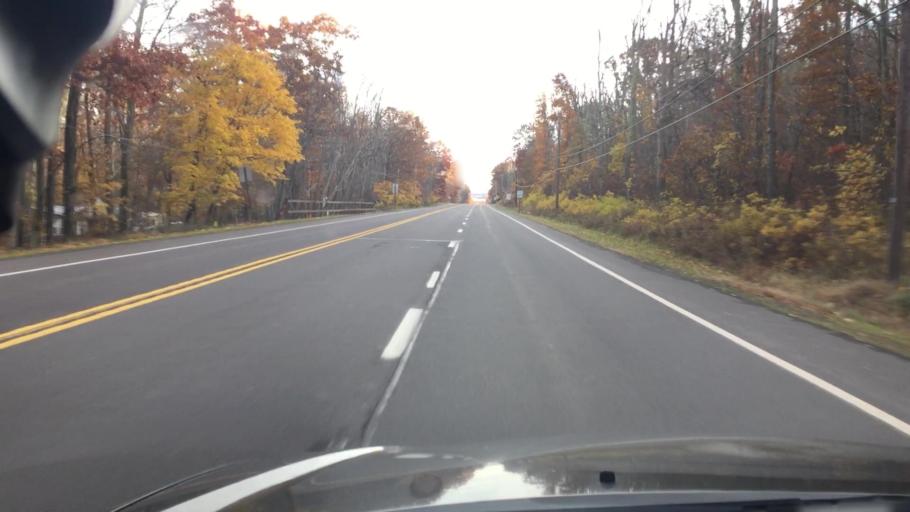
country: US
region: Pennsylvania
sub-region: Luzerne County
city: Mountain Top
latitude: 41.0996
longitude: -75.9294
